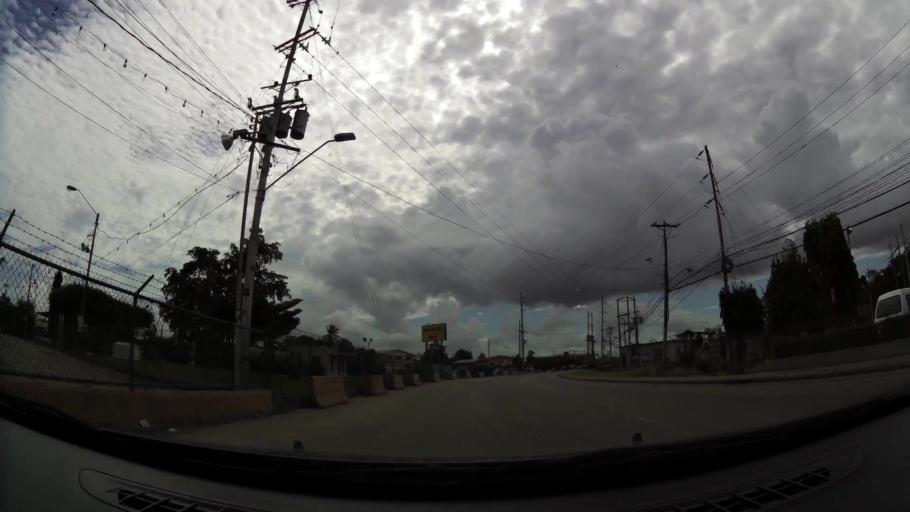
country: TT
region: Chaguanas
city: Chaguanas
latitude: 10.5112
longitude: -61.4082
